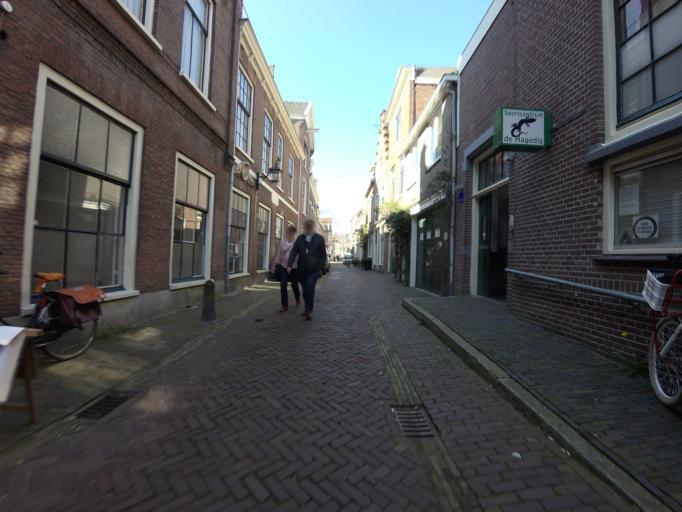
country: NL
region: North Holland
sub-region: Gemeente Haarlem
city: Haarlem
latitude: 52.3788
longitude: 4.6401
